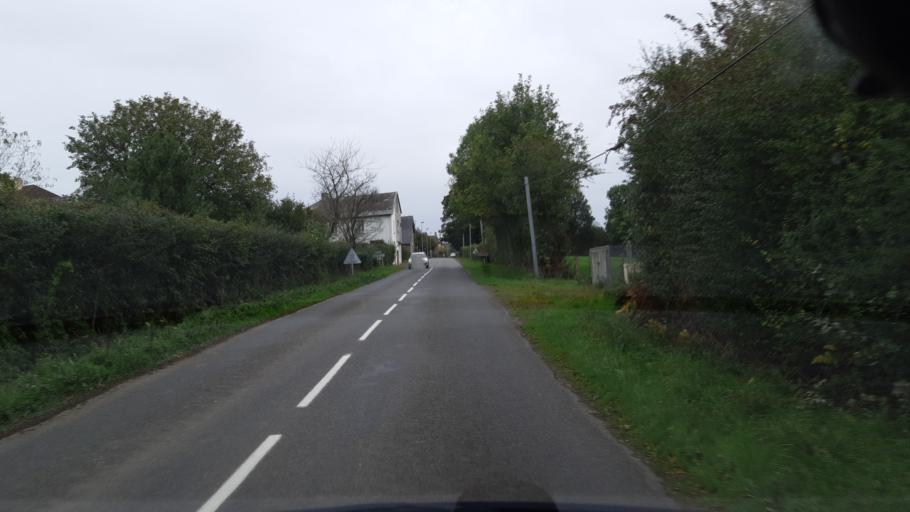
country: FR
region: Lower Normandy
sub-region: Departement de la Manche
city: Hambye
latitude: 48.9519
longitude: -1.2648
